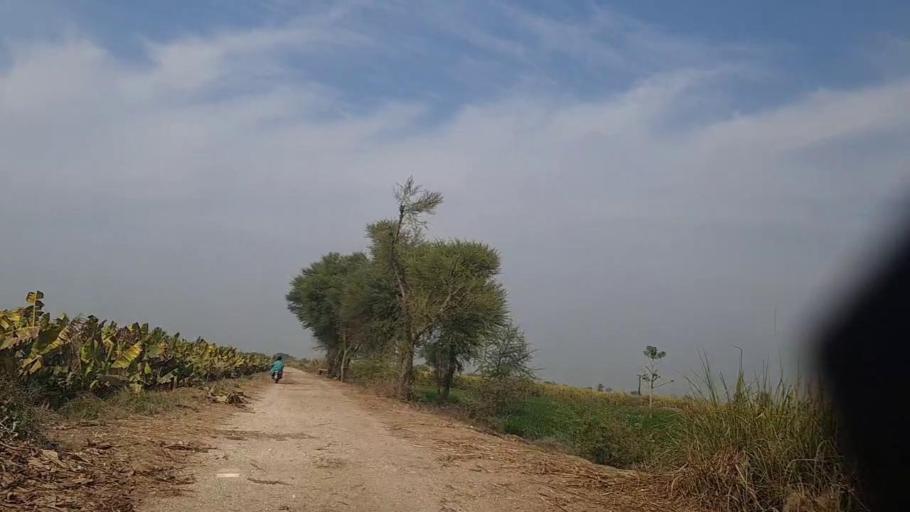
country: PK
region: Sindh
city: Daur
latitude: 26.4024
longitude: 68.2364
